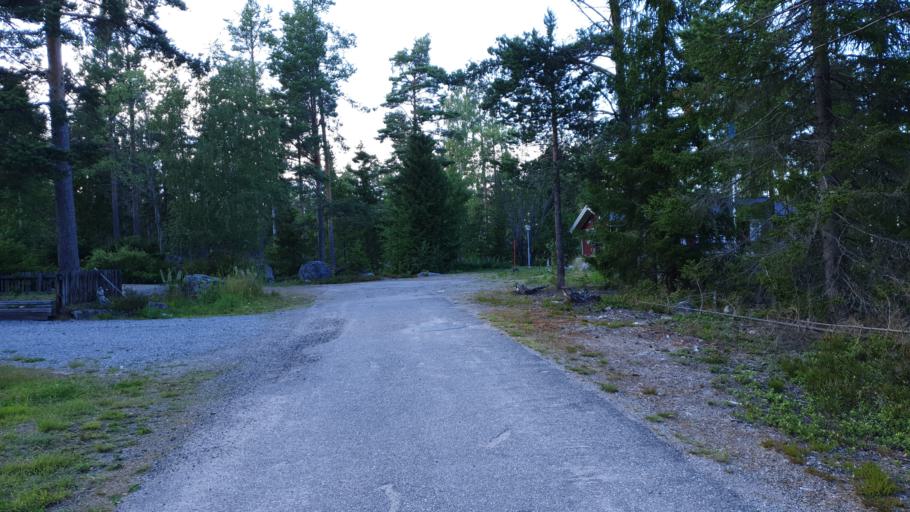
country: SE
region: Gaevleborg
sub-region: Soderhamns Kommun
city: Marielund
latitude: 61.4223
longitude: 17.1544
